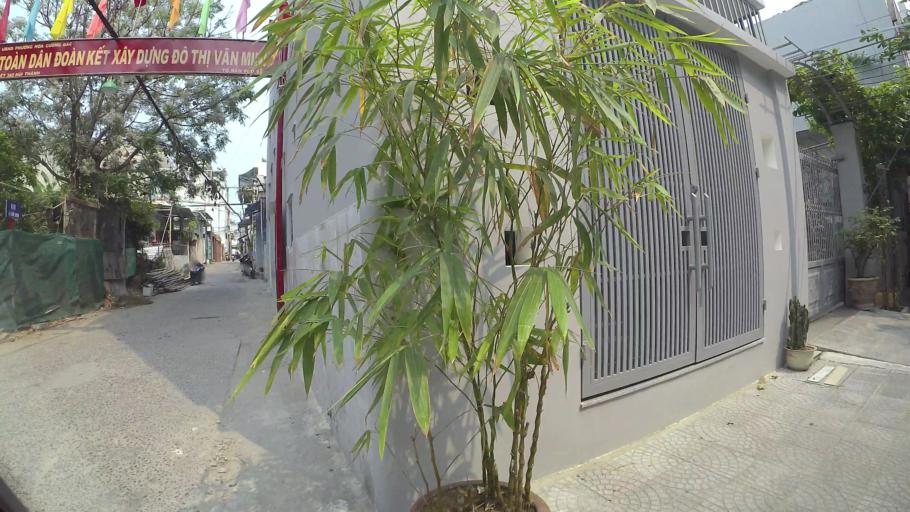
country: VN
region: Da Nang
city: Son Tra
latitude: 16.0389
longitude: 108.2189
